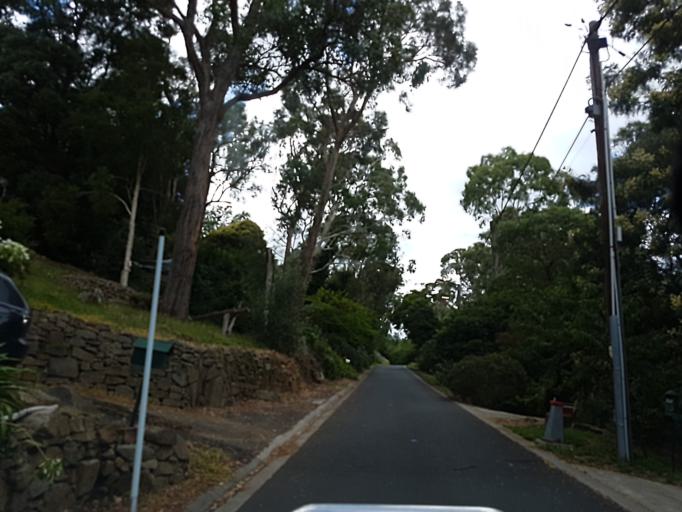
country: AU
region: Victoria
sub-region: Yarra Ranges
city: Tremont
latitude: -37.9050
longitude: 145.3219
